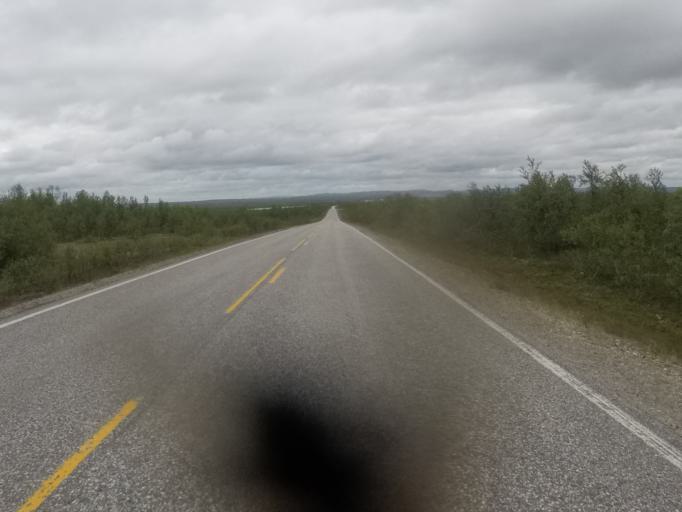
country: NO
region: Finnmark Fylke
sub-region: Kautokeino
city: Kautokeino
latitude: 68.7272
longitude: 23.3085
